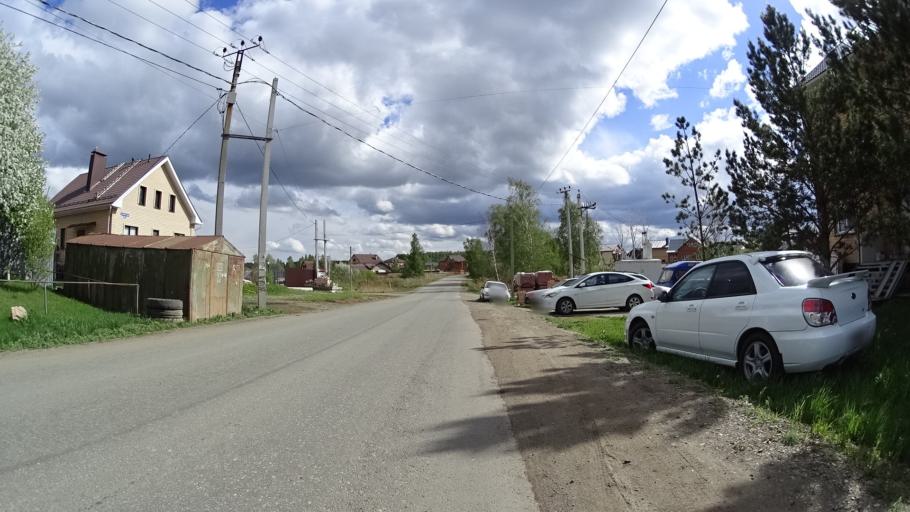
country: RU
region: Chelyabinsk
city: Sargazy
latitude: 55.1565
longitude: 61.2414
